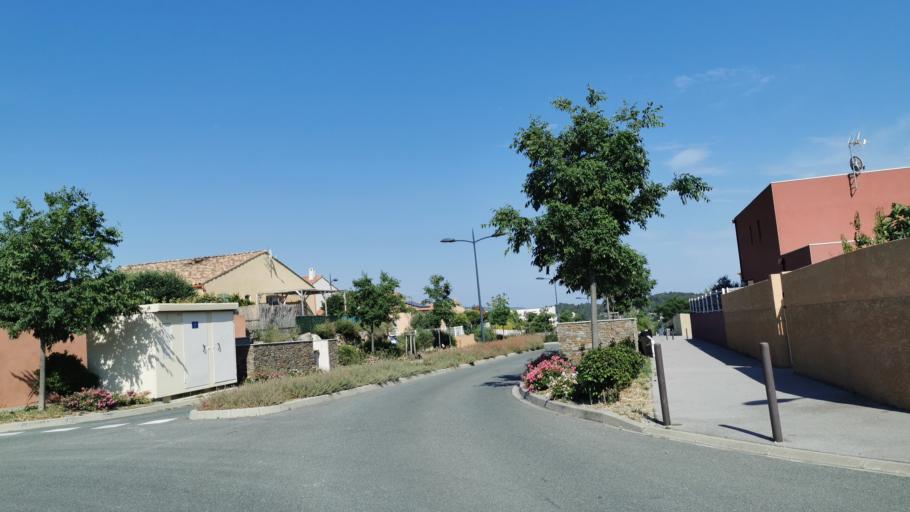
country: FR
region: Languedoc-Roussillon
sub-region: Departement de l'Aude
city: Peyriac-de-Mer
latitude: 43.1347
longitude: 2.9610
